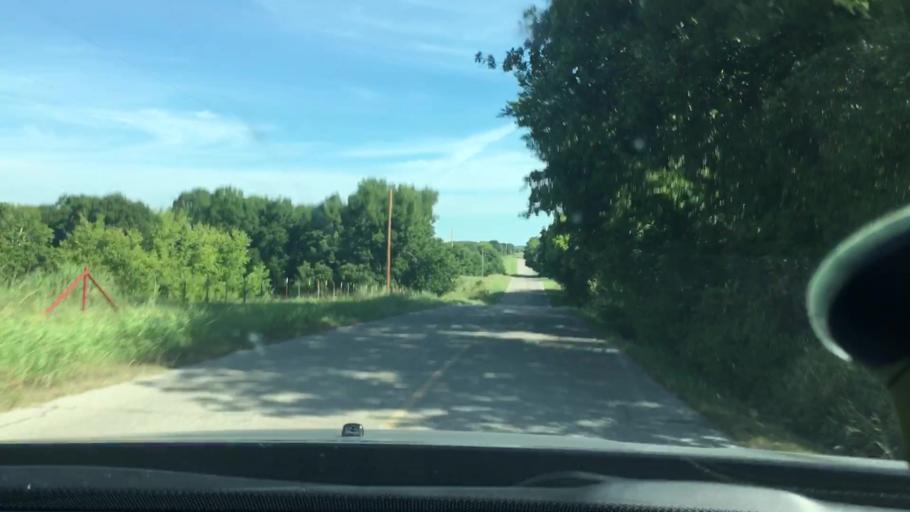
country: US
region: Oklahoma
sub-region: Carter County
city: Lone Grove
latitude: 34.3056
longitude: -97.2824
